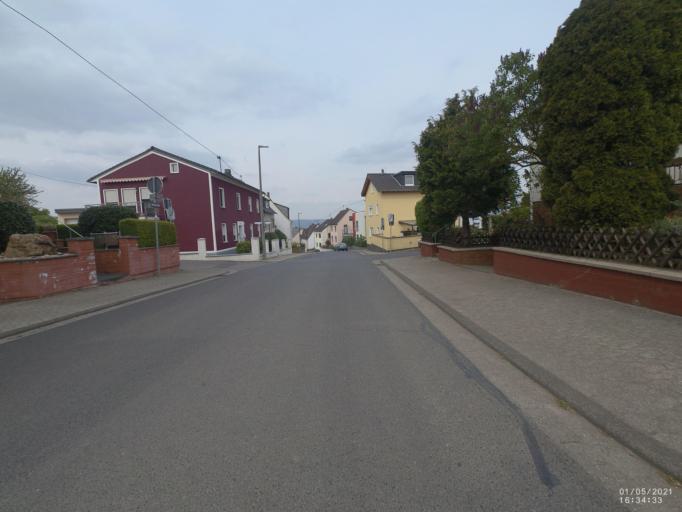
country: DE
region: Rheinland-Pfalz
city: Mulheim-Karlich
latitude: 50.3837
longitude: 7.4885
